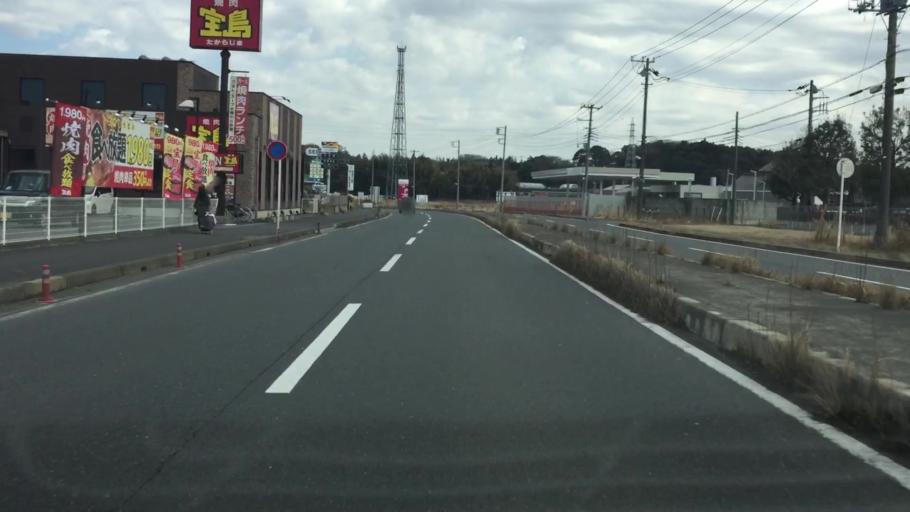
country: JP
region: Ibaraki
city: Ryugasaki
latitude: 35.8336
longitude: 140.1504
